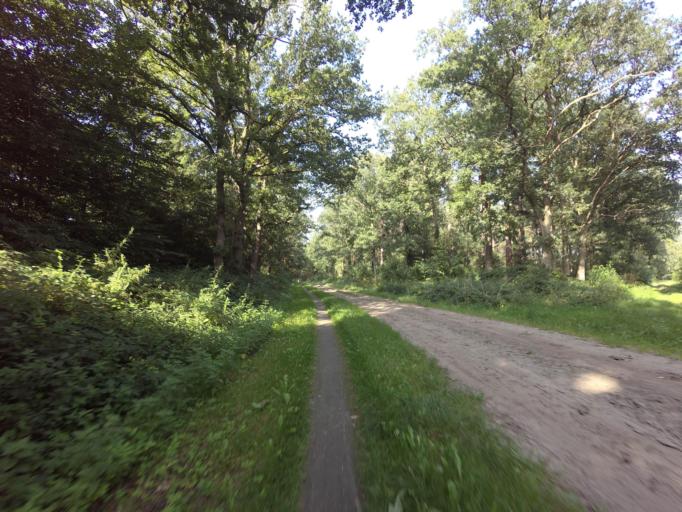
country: NL
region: Drenthe
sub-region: Gemeente Tynaarlo
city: Vries
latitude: 53.0623
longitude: 6.5067
